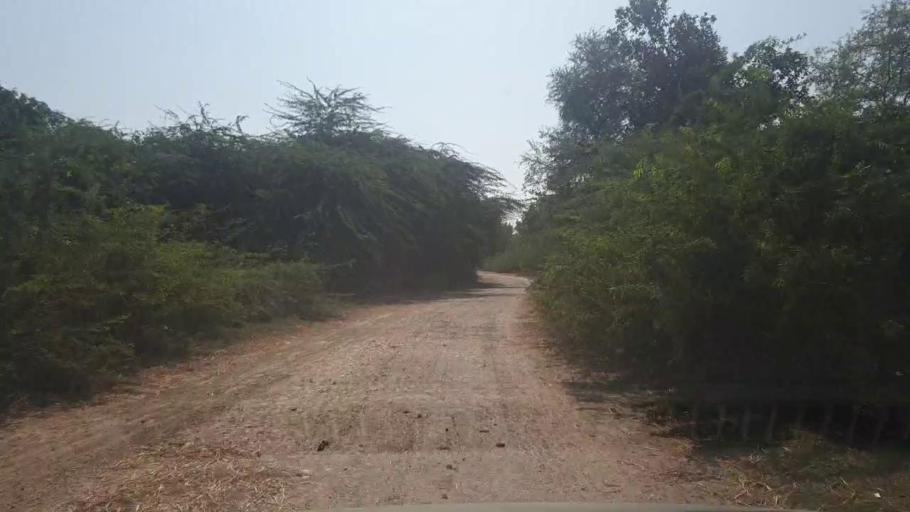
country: PK
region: Sindh
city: Badin
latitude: 24.6770
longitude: 68.8806
